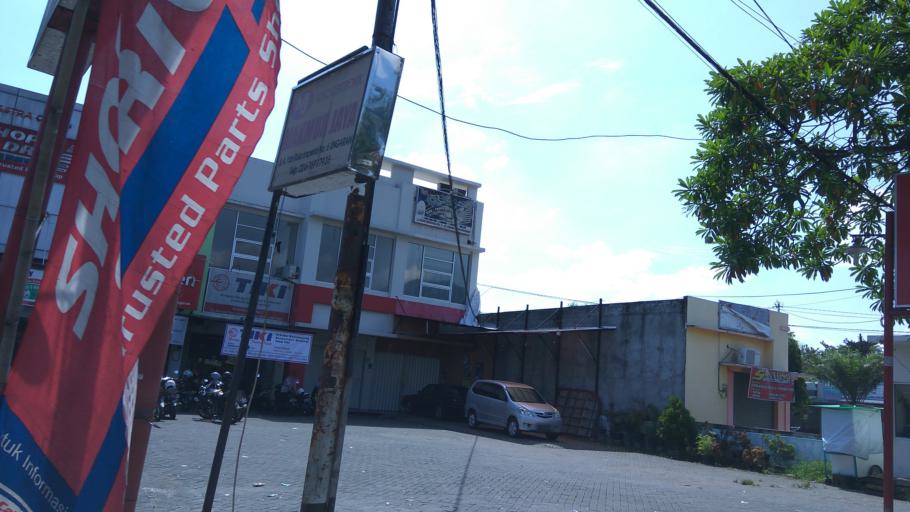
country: ID
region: Central Java
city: Ungaran
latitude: -7.1326
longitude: 110.4094
